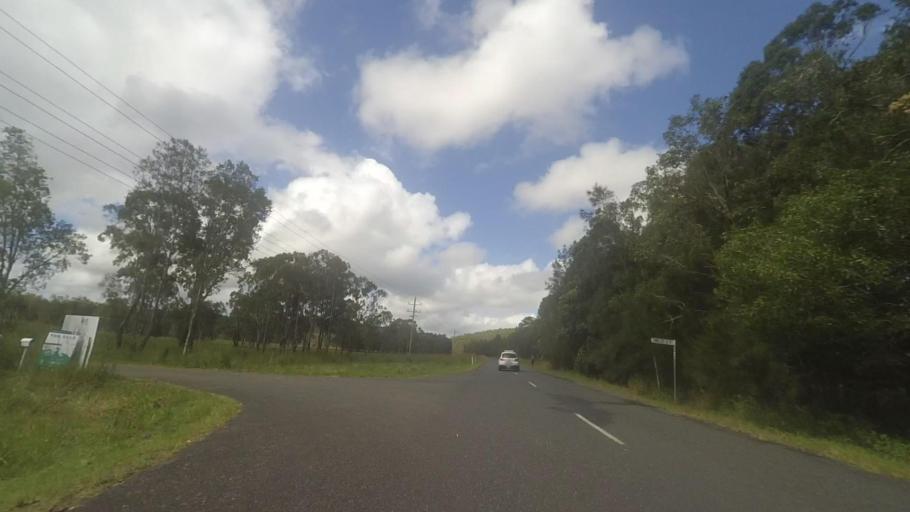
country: AU
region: New South Wales
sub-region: Great Lakes
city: Bulahdelah
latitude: -32.3880
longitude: 152.3347
